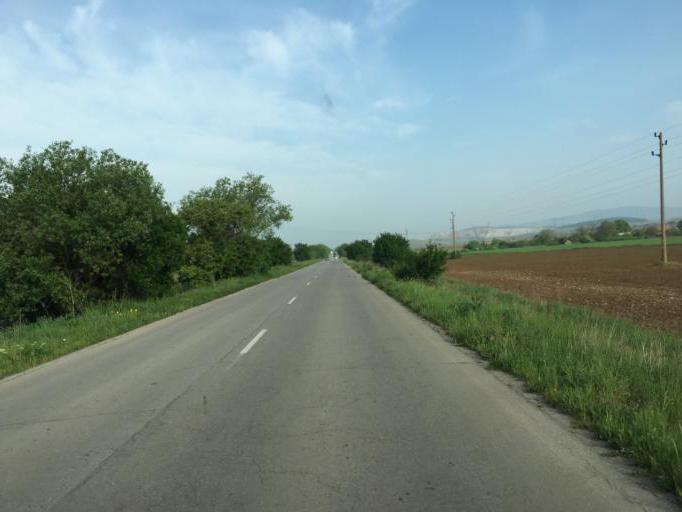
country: BG
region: Pernik
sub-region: Obshtina Radomir
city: Radomir
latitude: 42.4839
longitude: 23.0544
